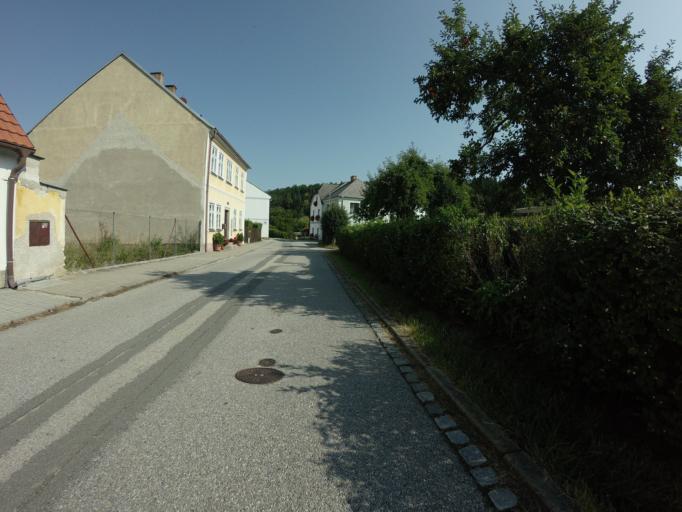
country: CZ
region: Jihocesky
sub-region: Okres Cesky Krumlov
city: Vyssi Brod
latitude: 48.6185
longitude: 14.3132
